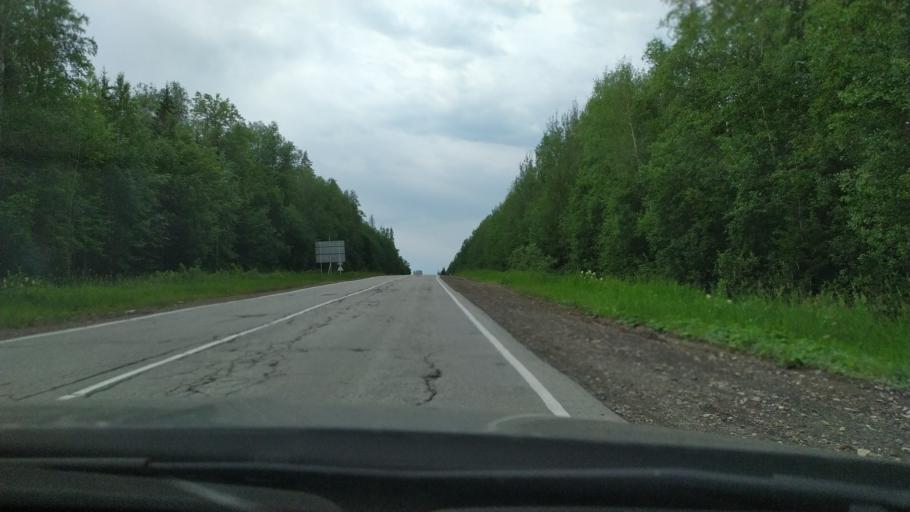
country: RU
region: Perm
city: Gremyachinsk
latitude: 58.4308
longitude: 57.8844
